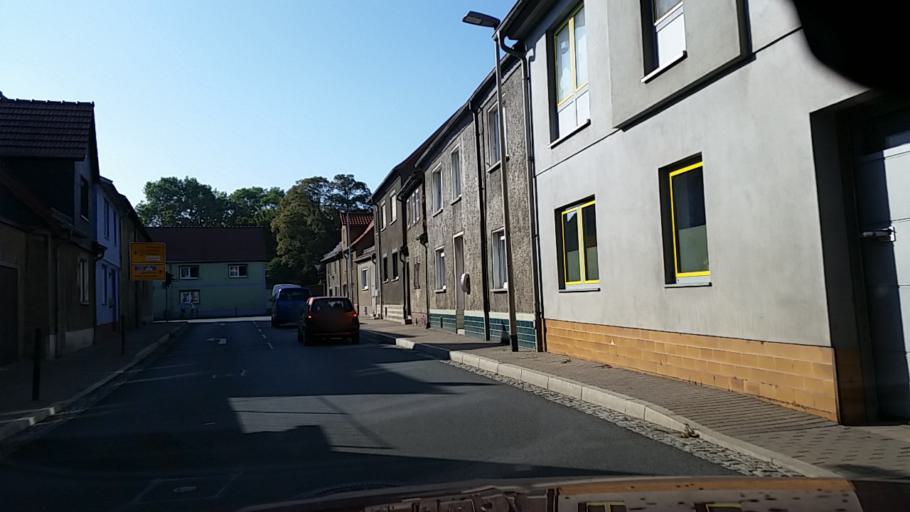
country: DE
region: Thuringia
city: Kolleda
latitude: 51.1865
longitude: 11.2412
